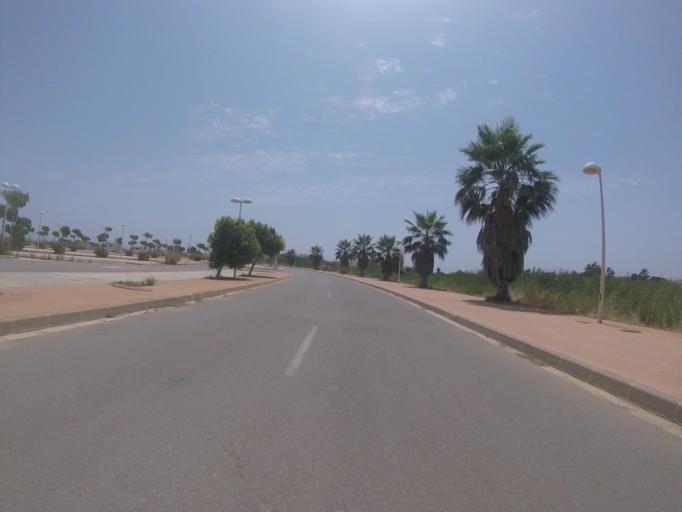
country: ES
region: Valencia
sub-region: Provincia de Castello
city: Orpesa/Oropesa del Mar
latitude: 40.1363
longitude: 0.1643
